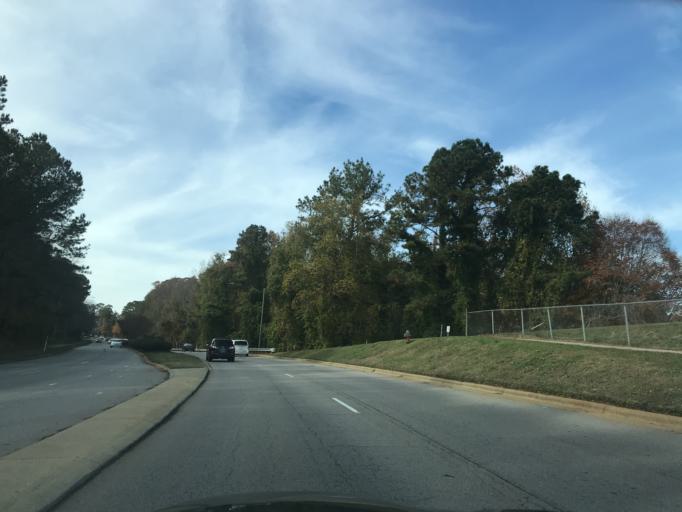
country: US
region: North Carolina
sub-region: Wake County
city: West Raleigh
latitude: 35.8565
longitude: -78.6627
